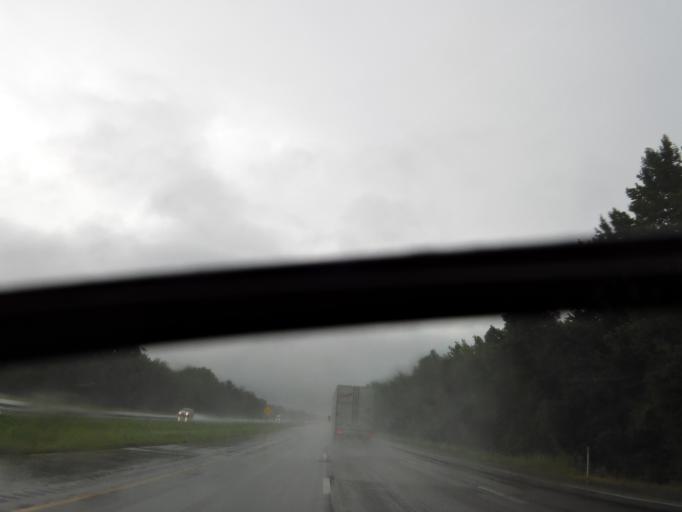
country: US
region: Illinois
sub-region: Williamson County
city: Johnston City
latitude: 37.8091
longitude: -88.9458
